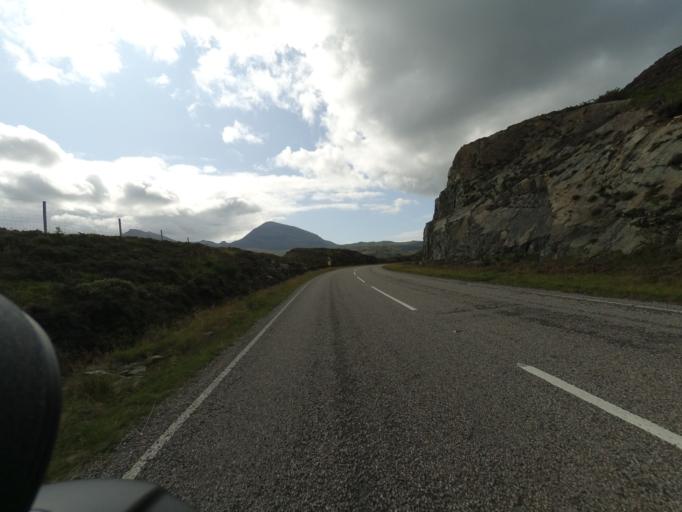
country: GB
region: Scotland
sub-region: Highland
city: Ullapool
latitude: 58.2569
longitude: -5.0286
